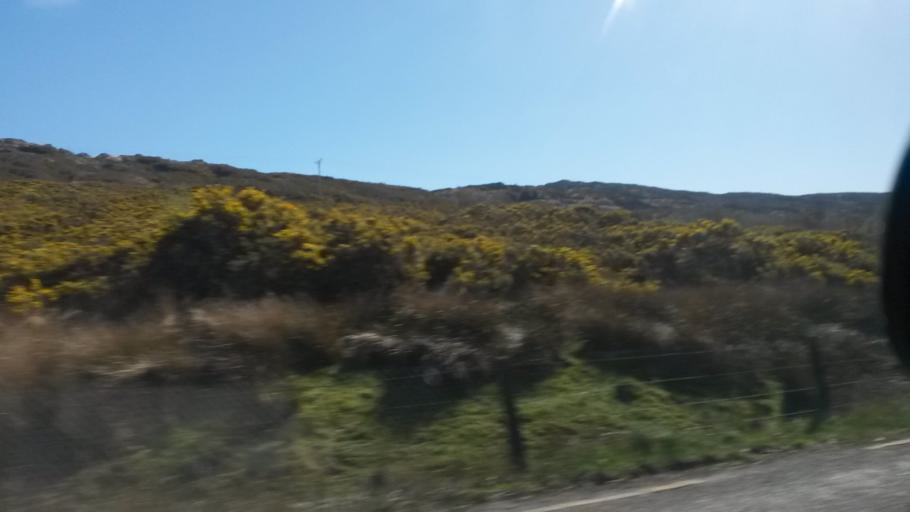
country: IE
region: Munster
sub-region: Ciarrai
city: Cill Airne
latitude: 51.9450
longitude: -9.3868
